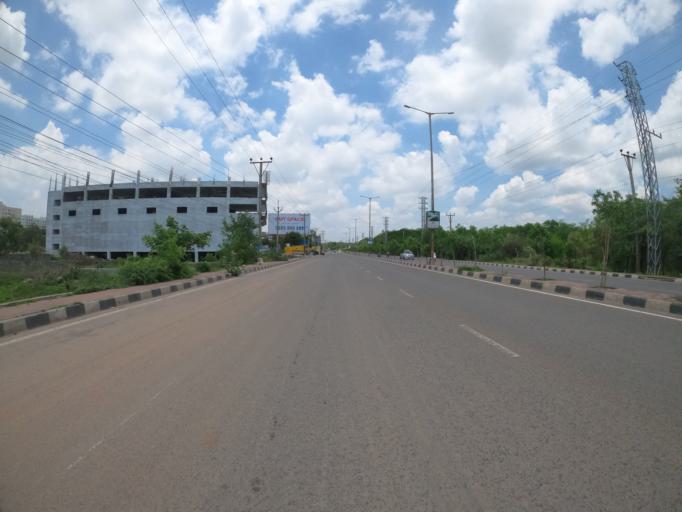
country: IN
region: Telangana
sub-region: Hyderabad
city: Hyderabad
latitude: 17.3512
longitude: 78.3662
